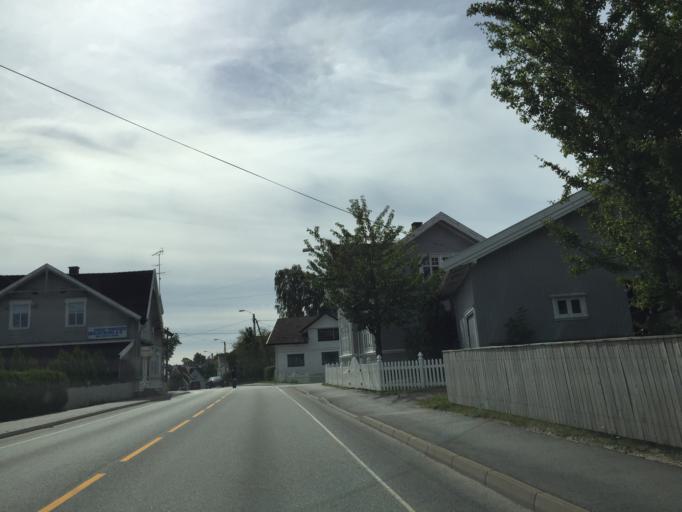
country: NO
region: Ostfold
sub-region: Fredrikstad
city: Fredrikstad
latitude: 59.1987
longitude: 10.9412
